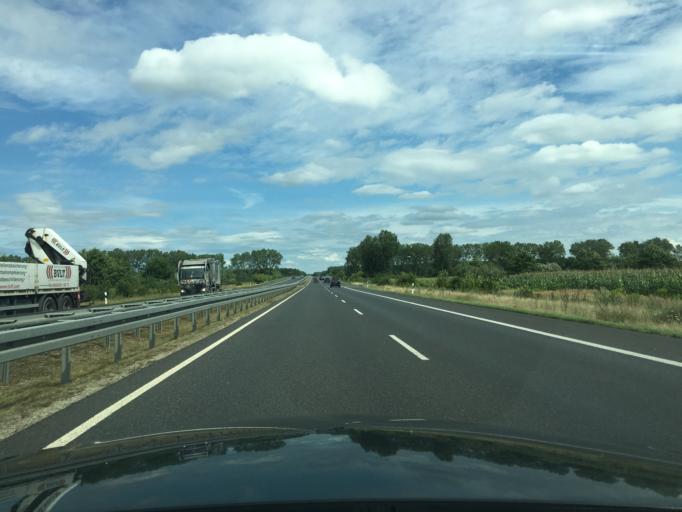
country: DE
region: Brandenburg
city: Oranienburg
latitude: 52.7718
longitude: 13.2153
